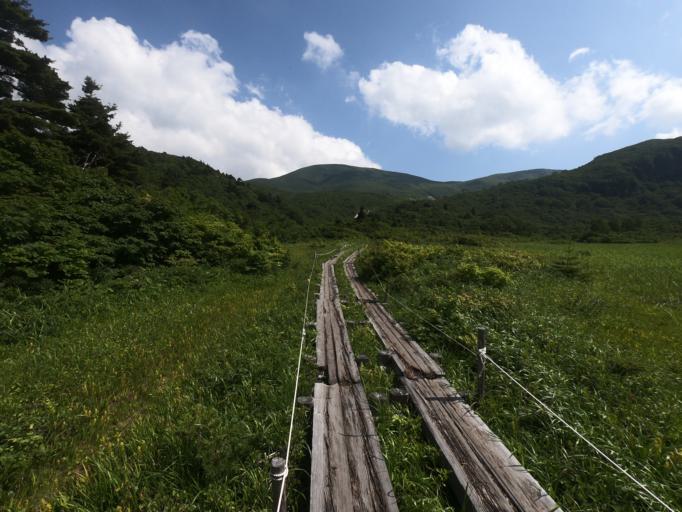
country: JP
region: Akita
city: Yuzawa
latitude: 38.9764
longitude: 140.7776
